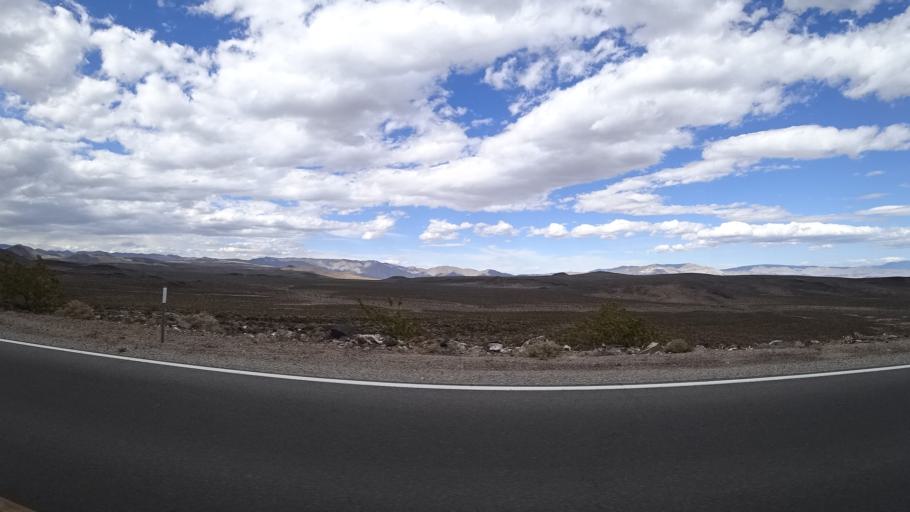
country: US
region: California
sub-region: Inyo County
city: Lone Pine
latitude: 36.3752
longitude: -117.5898
